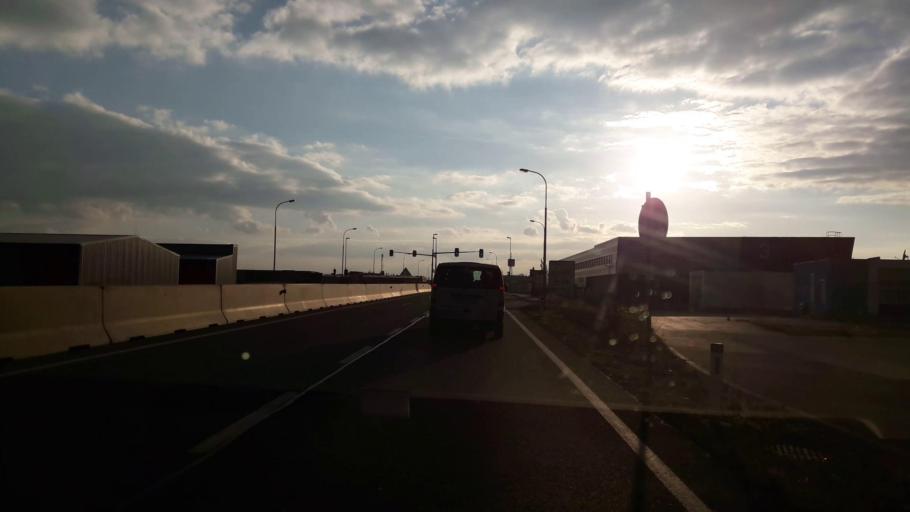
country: AT
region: Lower Austria
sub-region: Politischer Bezirk Mistelbach
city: Grossebersdorf
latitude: 48.3427
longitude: 16.4688
